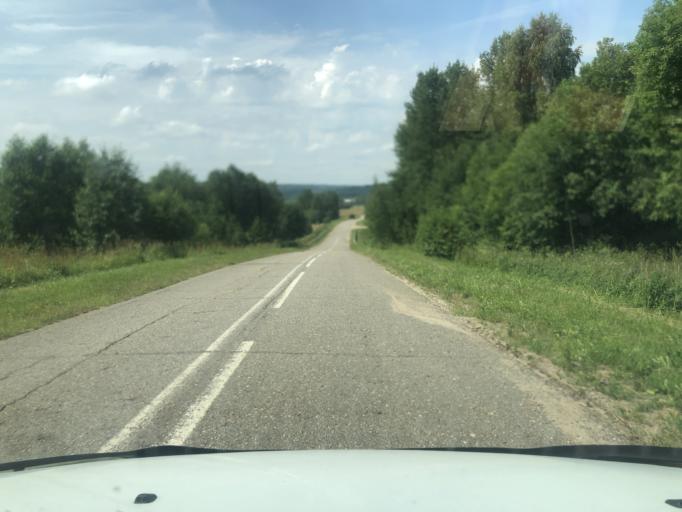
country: RU
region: Jaroslavl
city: Pereslavl'-Zalesskiy
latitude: 57.0405
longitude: 38.8765
